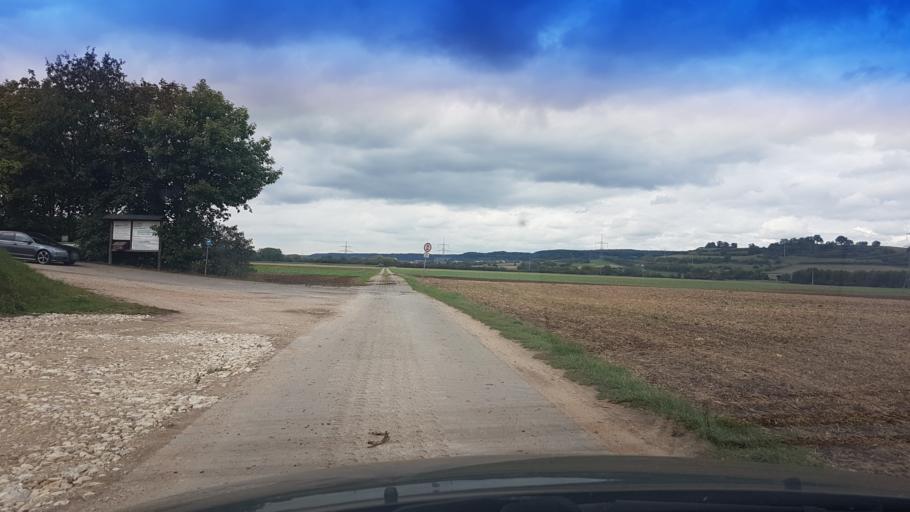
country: DE
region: Bavaria
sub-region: Upper Franconia
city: Viereth-Trunstadt
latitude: 49.9310
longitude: 10.7706
